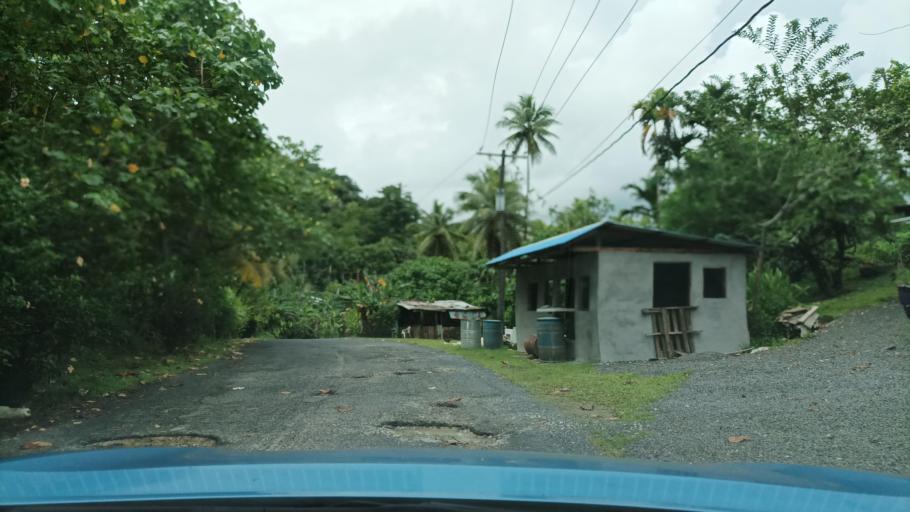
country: FM
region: Pohnpei
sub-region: Madolenihm Municipality
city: Madolenihm Municipality Government
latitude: 6.9211
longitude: 158.3200
